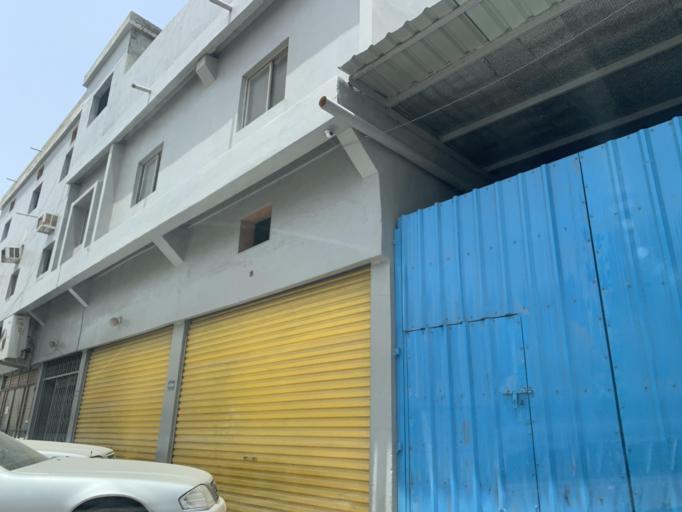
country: BH
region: Northern
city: Ar Rifa'
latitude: 26.1372
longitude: 50.5853
